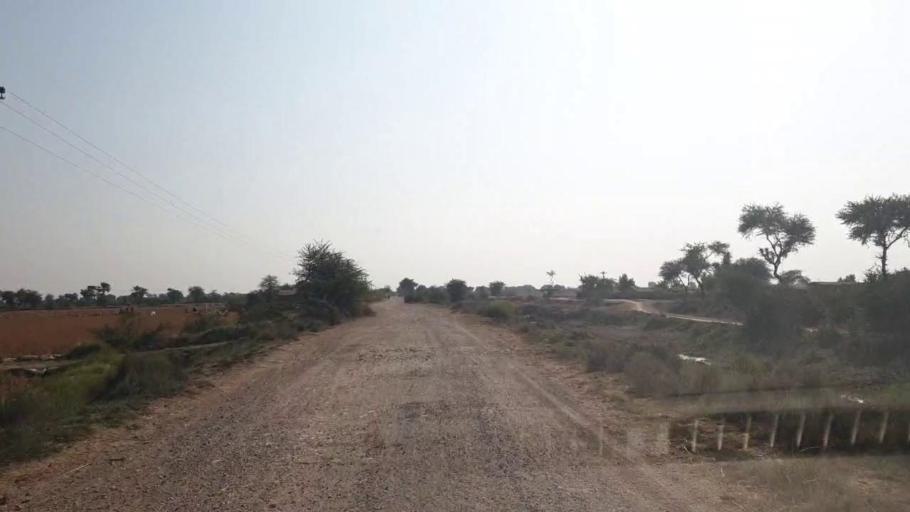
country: PK
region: Sindh
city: Kario
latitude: 24.9060
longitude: 68.6489
